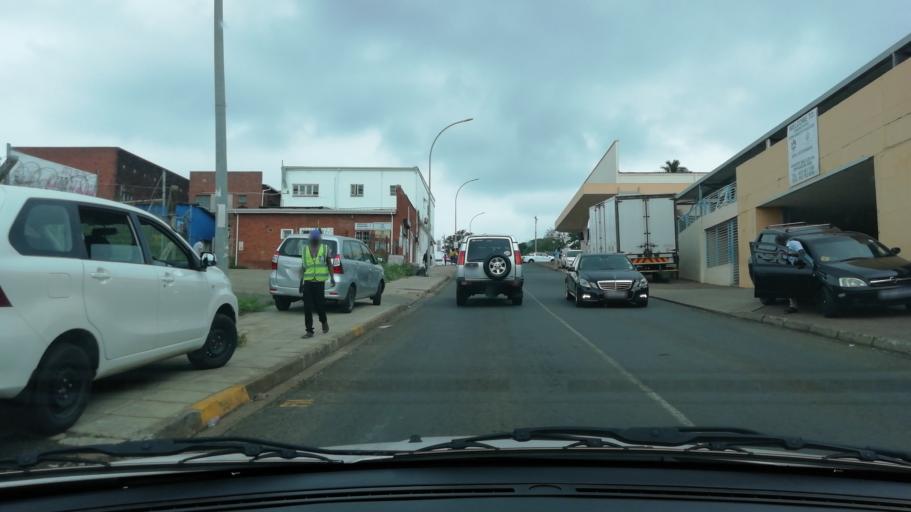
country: ZA
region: KwaZulu-Natal
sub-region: uThungulu District Municipality
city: Empangeni
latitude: -28.7420
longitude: 31.8916
